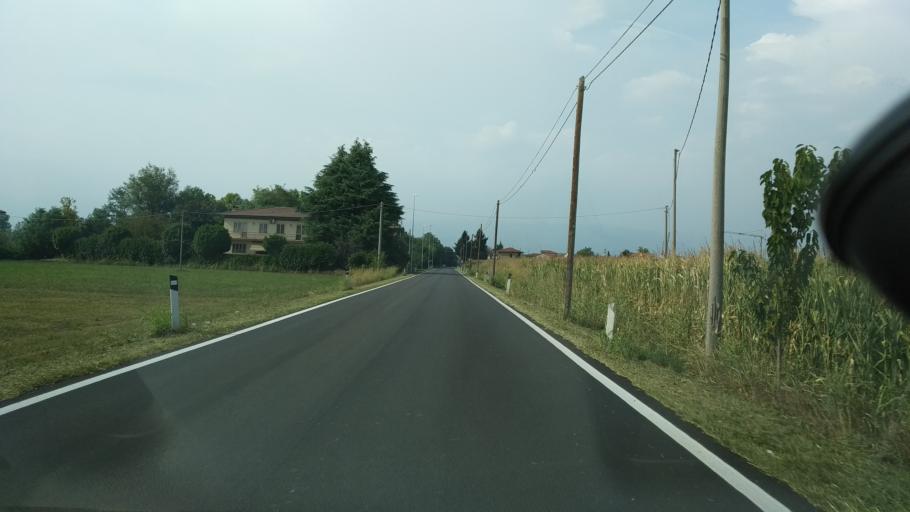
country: IT
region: Veneto
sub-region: Provincia di Vicenza
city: Tezze
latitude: 45.6777
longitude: 11.7082
